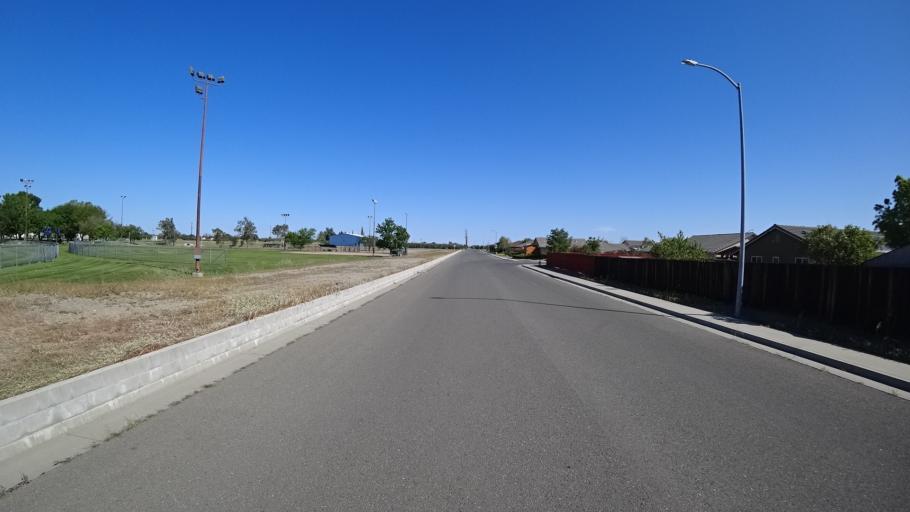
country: US
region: California
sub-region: Glenn County
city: Orland
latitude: 39.7374
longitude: -122.1688
